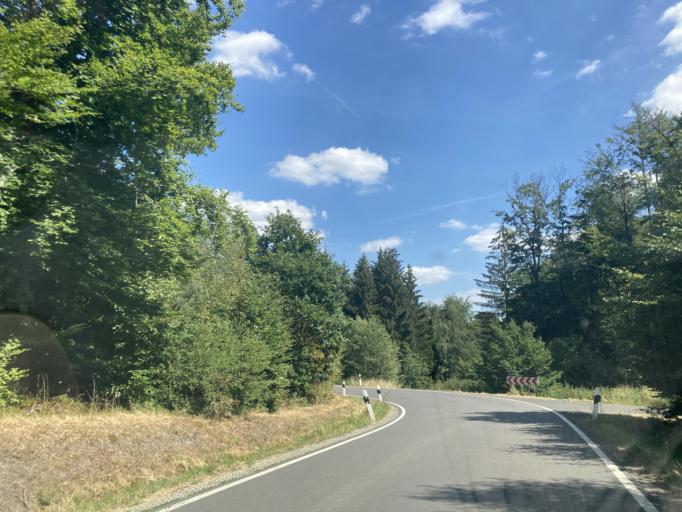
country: DE
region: Hesse
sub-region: Regierungsbezirk Kassel
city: Ottrau
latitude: 50.7320
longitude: 9.3855
